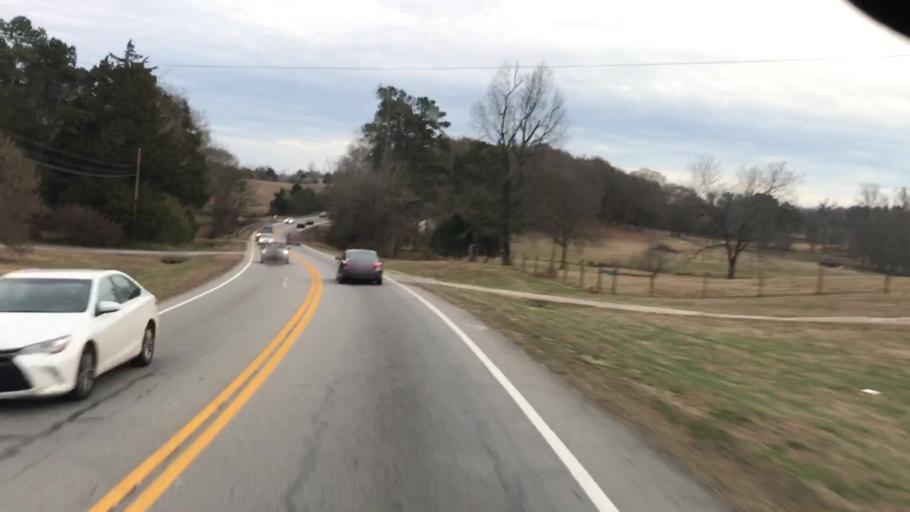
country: US
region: Georgia
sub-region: Barrow County
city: Auburn
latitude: 34.0270
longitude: -83.7730
